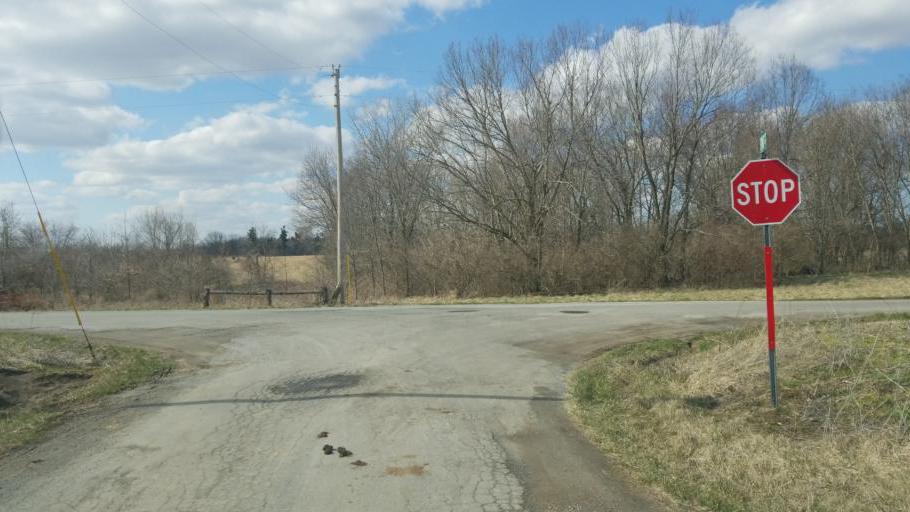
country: US
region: Ohio
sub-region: Highland County
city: Greenfield
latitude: 39.3034
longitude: -83.4260
